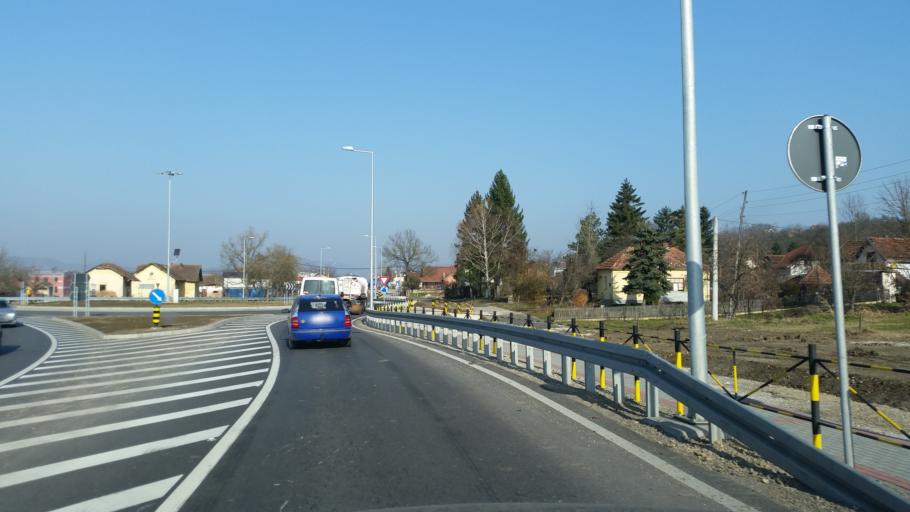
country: RS
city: Prislonica
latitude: 43.9182
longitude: 20.4080
